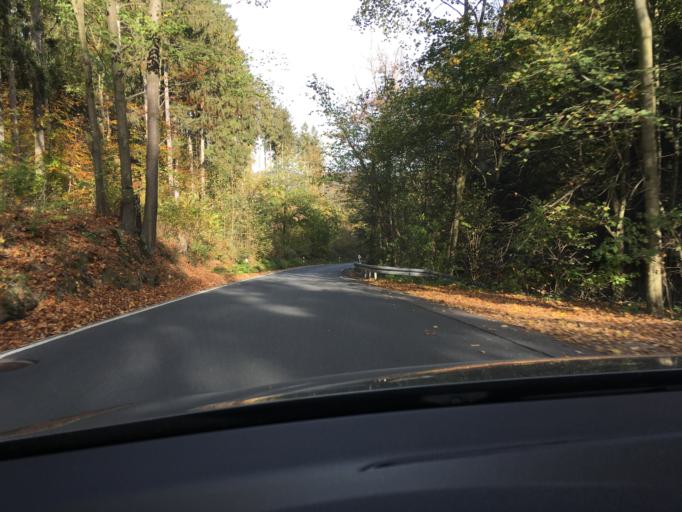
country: DE
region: Saxony
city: Glashutte
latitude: 50.8469
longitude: 13.7964
